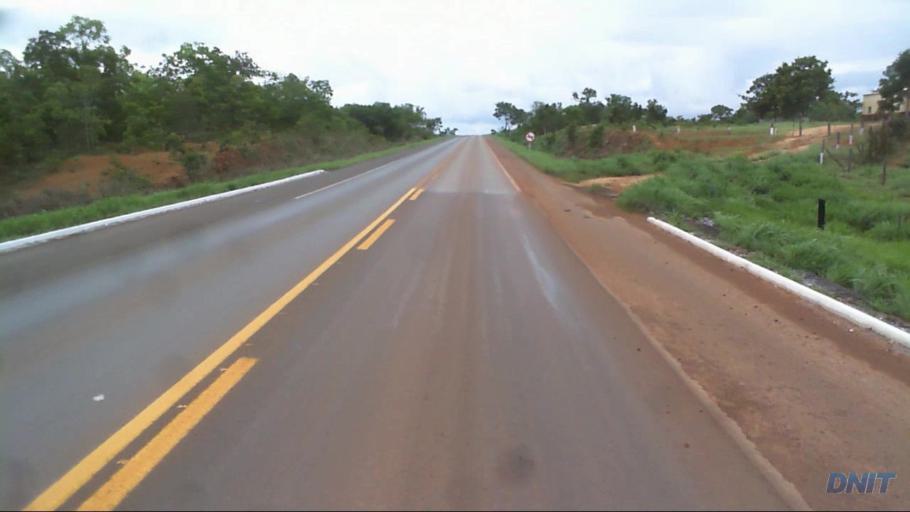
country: BR
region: Goias
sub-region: Padre Bernardo
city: Padre Bernardo
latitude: -15.1530
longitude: -48.3321
